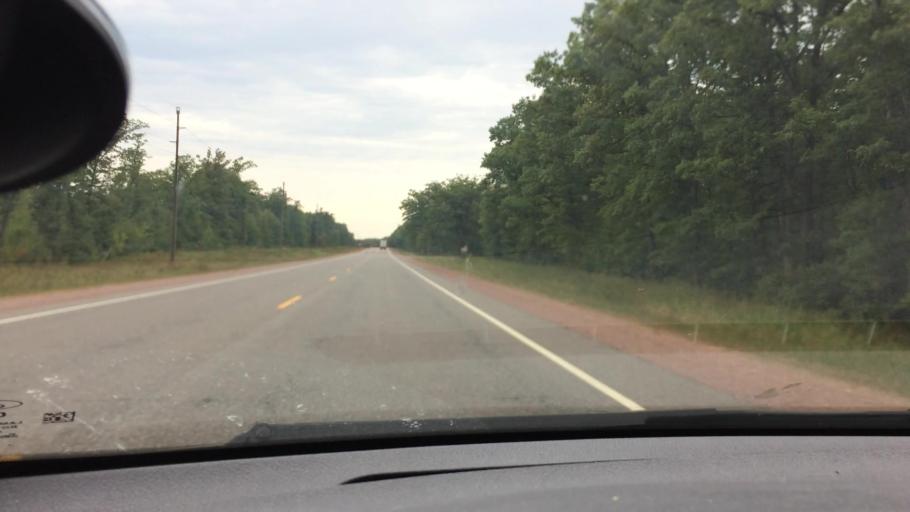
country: US
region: Wisconsin
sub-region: Clark County
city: Neillsville
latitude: 44.5771
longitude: -90.7360
